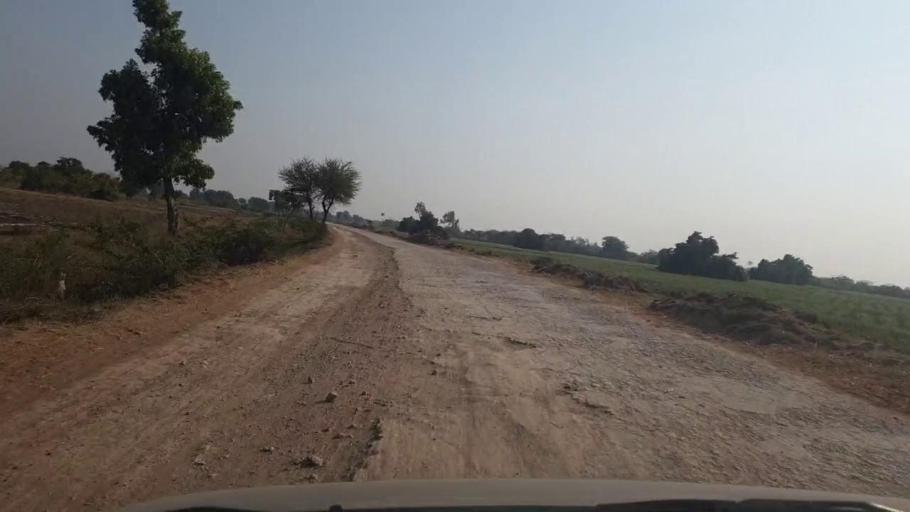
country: PK
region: Sindh
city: Digri
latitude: 25.2548
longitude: 69.1824
